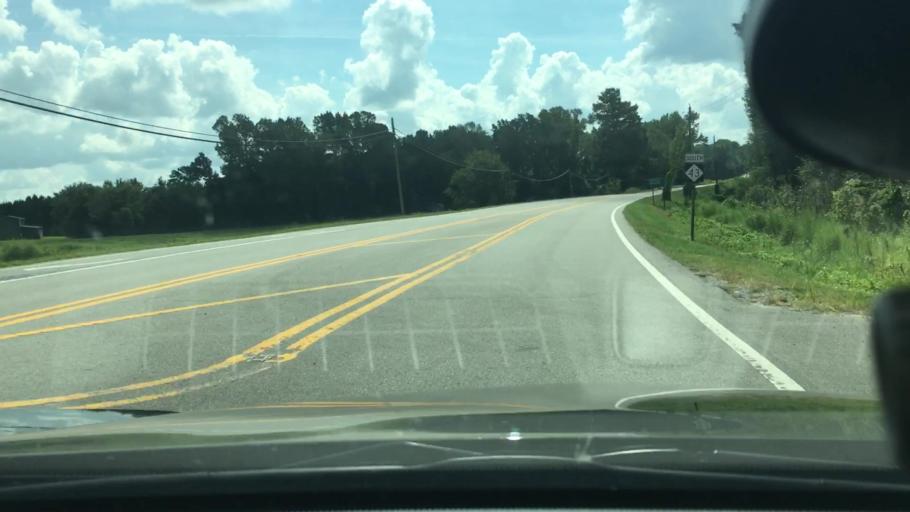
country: US
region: North Carolina
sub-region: Pitt County
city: Farmville
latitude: 35.6931
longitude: -77.4985
